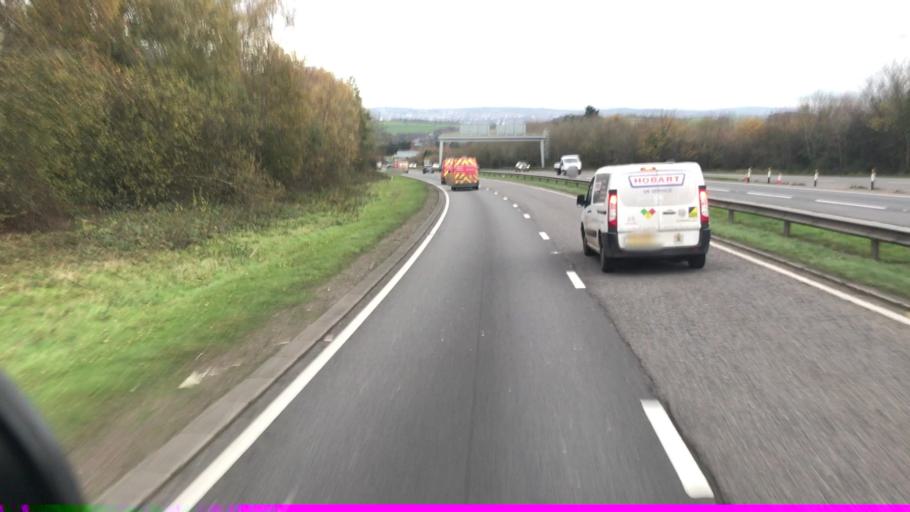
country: GB
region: England
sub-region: Devon
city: Exminster
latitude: 50.6499
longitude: -3.5418
